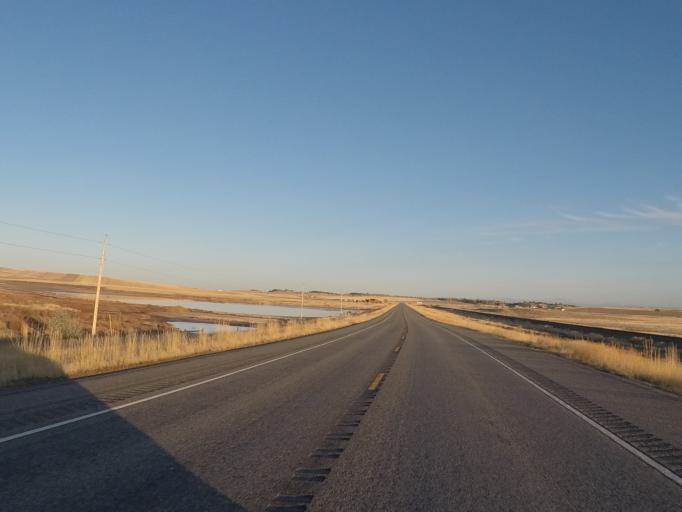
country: US
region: Montana
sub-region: Yellowstone County
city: Billings
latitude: 45.9369
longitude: -108.6962
